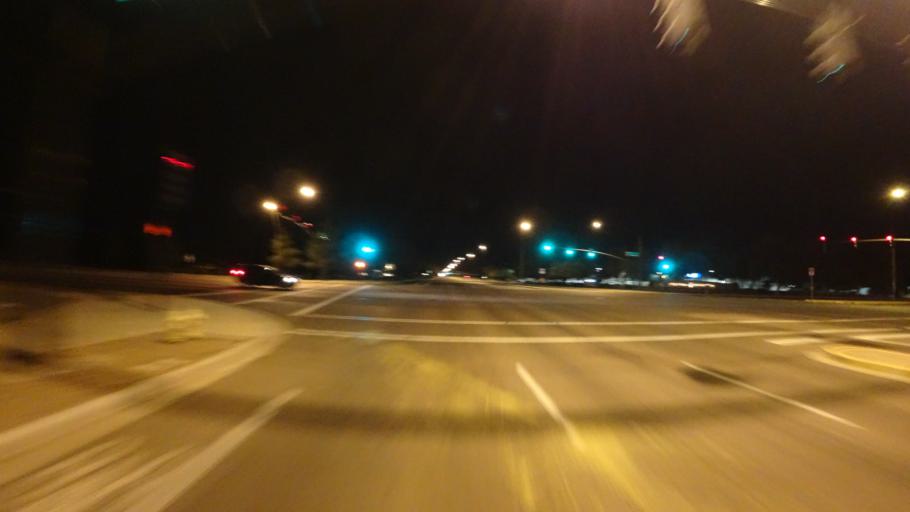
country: US
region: Arizona
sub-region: Maricopa County
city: Queen Creek
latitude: 33.2785
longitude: -111.6861
